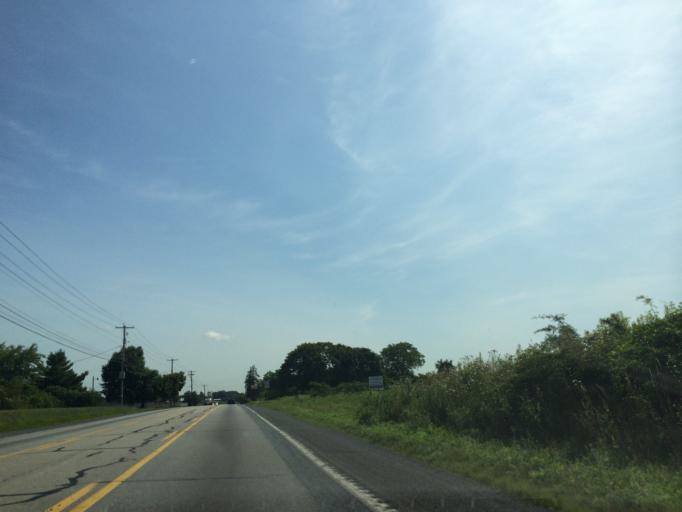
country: US
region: Pennsylvania
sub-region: Berks County
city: Blandon
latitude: 40.4592
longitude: -75.8776
